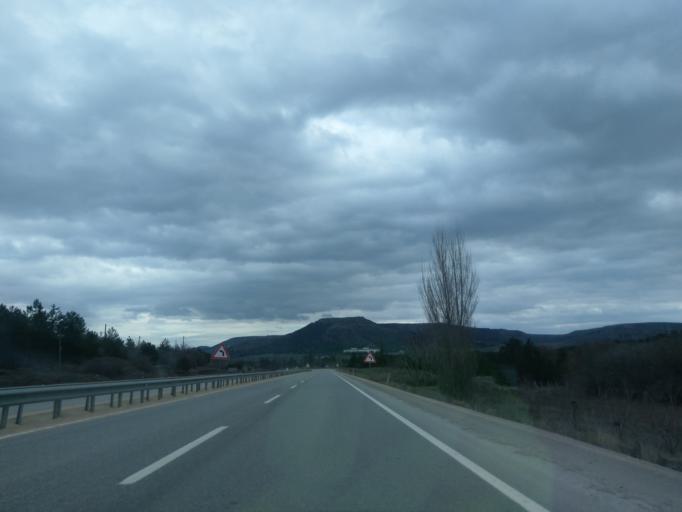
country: TR
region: Eskisehir
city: Eskisehir
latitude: 39.7409
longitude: 30.4180
